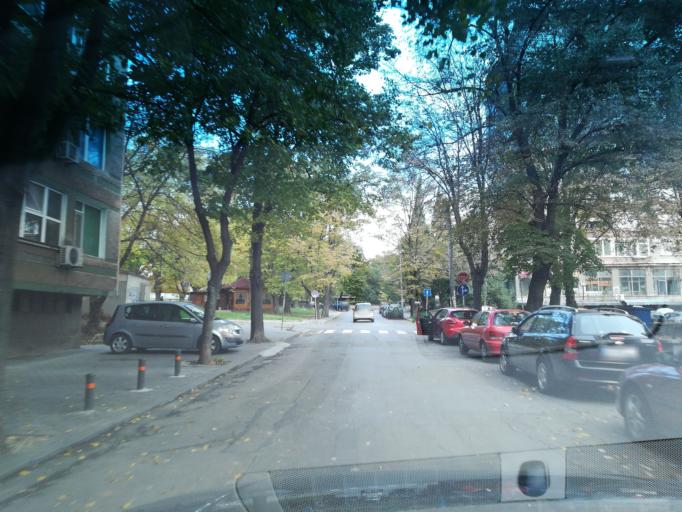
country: BG
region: Stara Zagora
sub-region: Obshtina Stara Zagora
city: Stara Zagora
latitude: 42.4319
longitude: 25.6276
